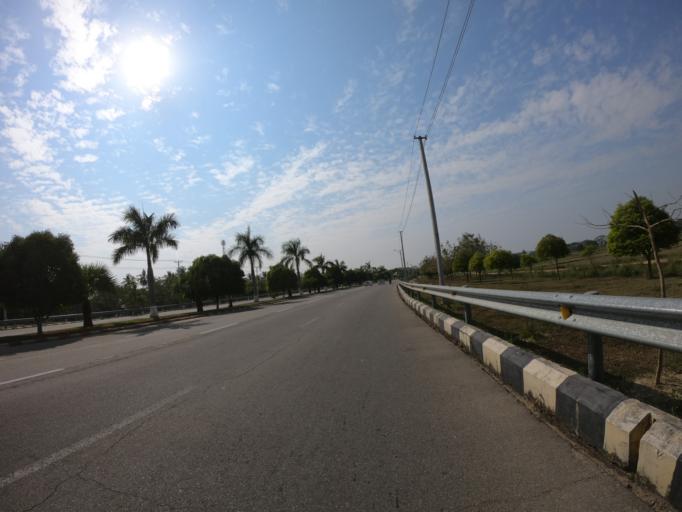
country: MM
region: Mandalay
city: Nay Pyi Taw
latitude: 19.6515
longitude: 96.1441
